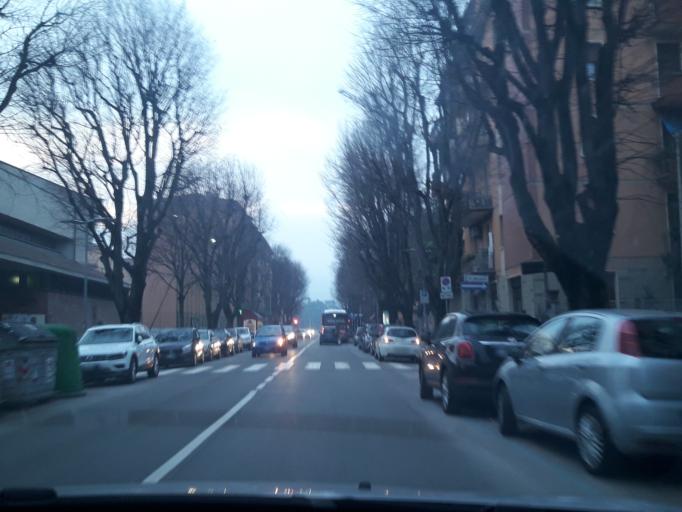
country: IT
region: Emilia-Romagna
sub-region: Provincia di Bologna
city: Bologna
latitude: 44.5021
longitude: 11.3120
